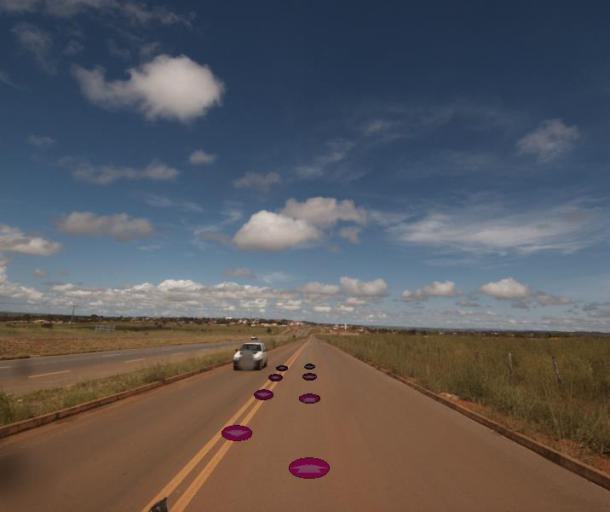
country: BR
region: Federal District
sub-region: Brasilia
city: Brasilia
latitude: -15.7455
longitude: -48.3192
